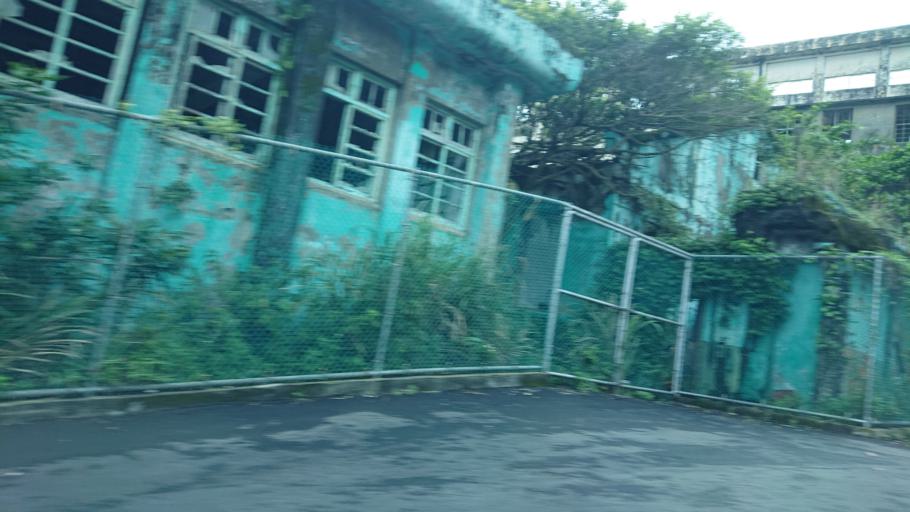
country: TW
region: Taiwan
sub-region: Keelung
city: Keelung
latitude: 25.1211
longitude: 121.8629
